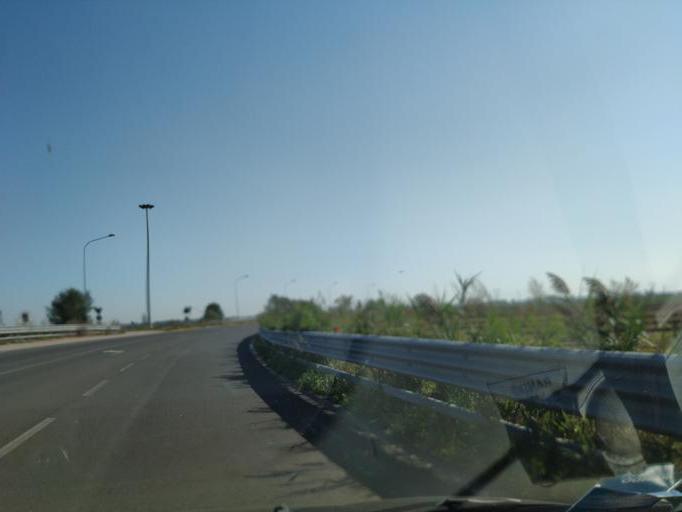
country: IT
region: Emilia-Romagna
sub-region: Provincia di Bologna
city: San Giovanni in Persiceto
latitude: 44.6767
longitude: 11.1944
